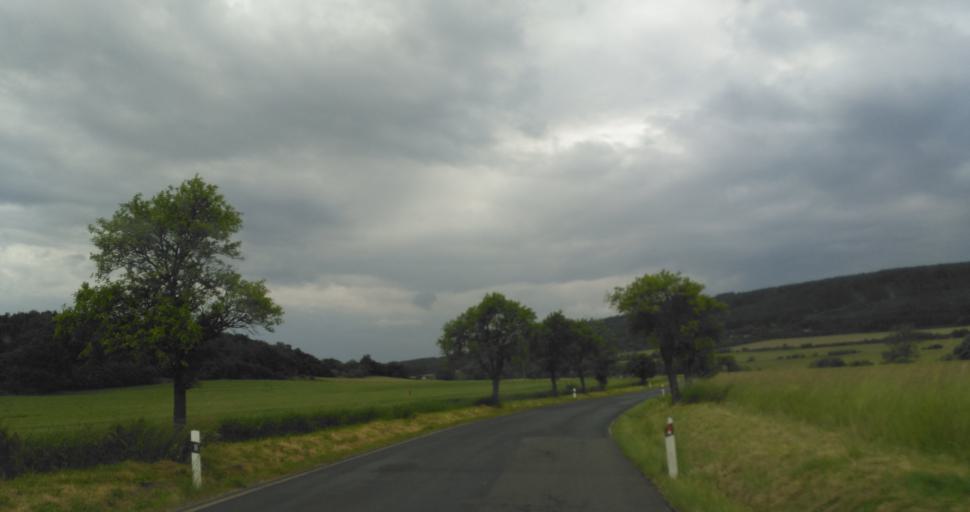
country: CZ
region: Central Bohemia
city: Hostomice
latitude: 49.8135
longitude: 14.0313
